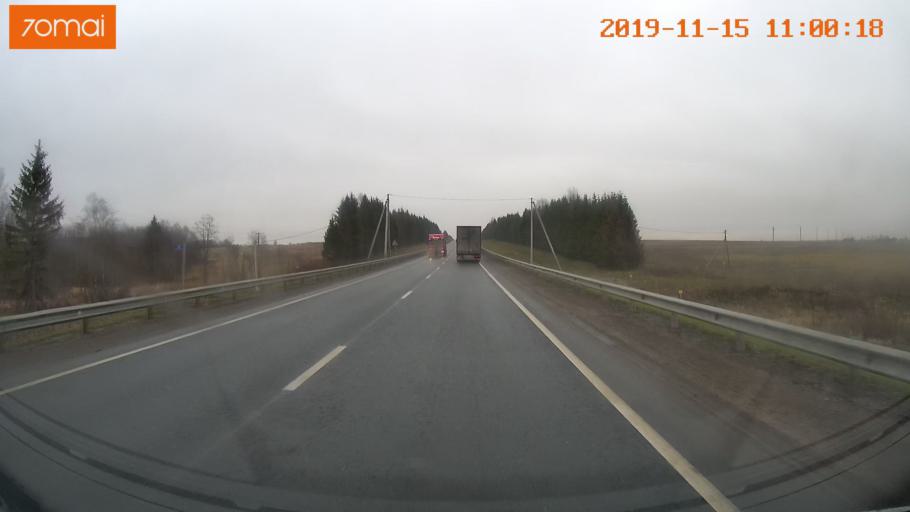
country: RU
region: Vologda
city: Chebsara
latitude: 59.1378
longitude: 38.8960
